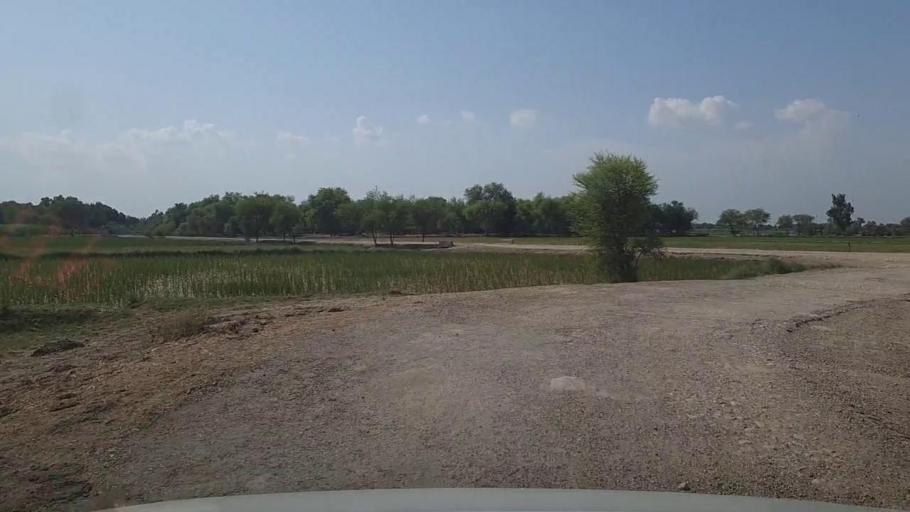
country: PK
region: Sindh
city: Khairpur
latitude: 28.1209
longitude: 69.6102
